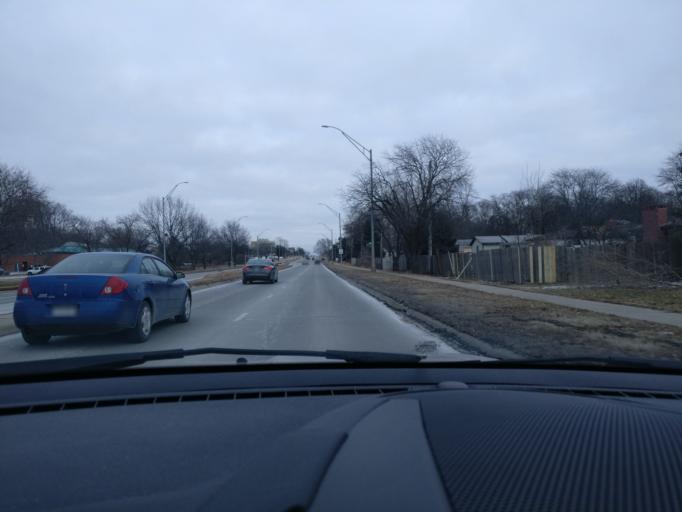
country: US
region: Nebraska
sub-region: Lancaster County
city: Lincoln
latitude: 40.8134
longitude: -96.6157
